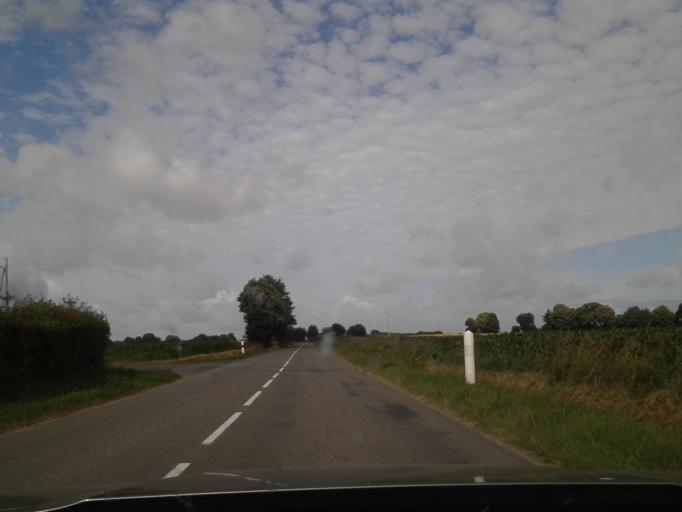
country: FR
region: Pays de la Loire
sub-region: Departement de la Mayenne
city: Ambrieres-les-Vallees
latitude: 48.4271
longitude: -0.6863
